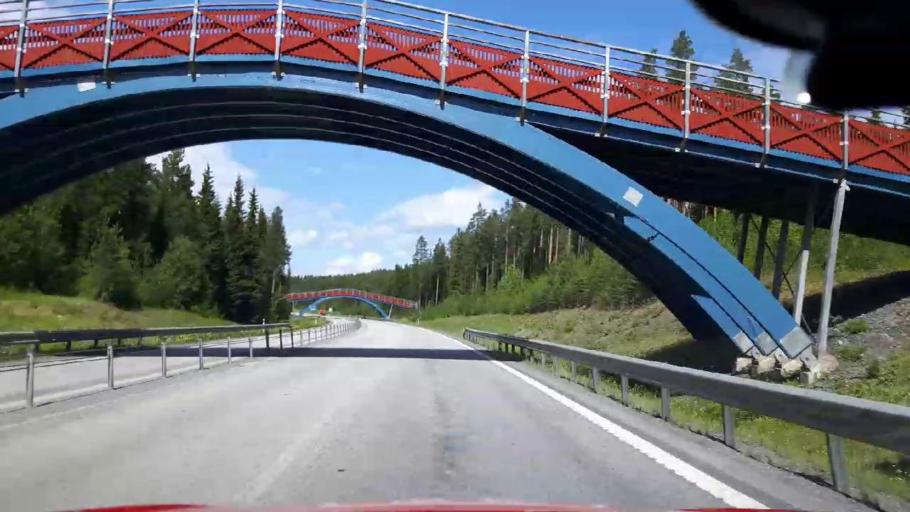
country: SE
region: Jaemtland
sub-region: OEstersunds Kommun
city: Ostersund
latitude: 63.1915
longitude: 14.6902
